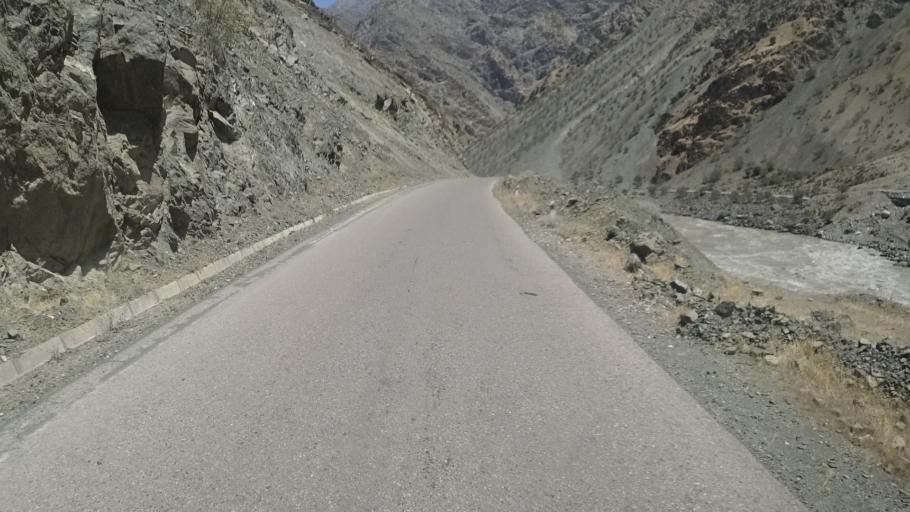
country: AF
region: Badakhshan
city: Deh Khwahan
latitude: 37.9390
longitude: 70.2679
